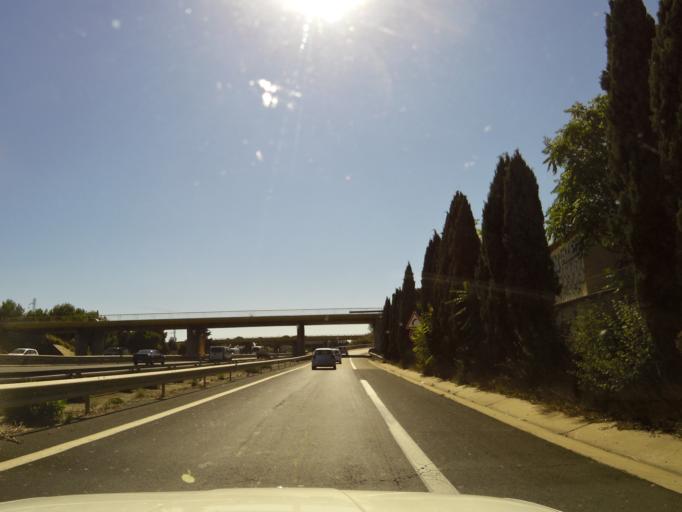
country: FR
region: Languedoc-Roussillon
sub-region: Departement de l'Herault
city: Lattes
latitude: 43.5750
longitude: 3.8766
